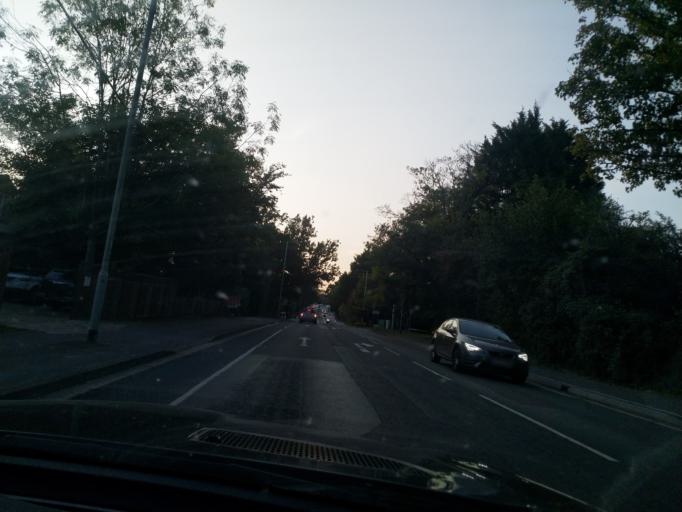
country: GB
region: England
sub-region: Kent
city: Leysdown-on-Sea
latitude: 51.4224
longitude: 0.8630
